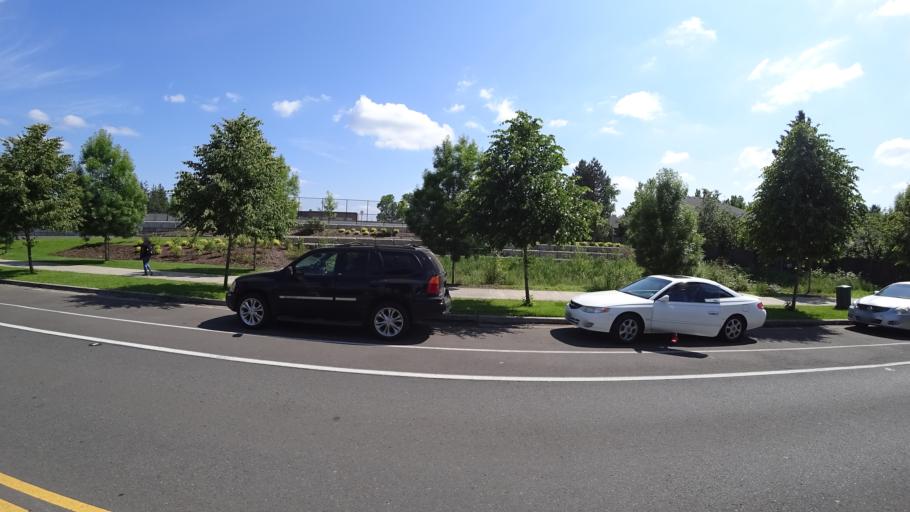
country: US
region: Oregon
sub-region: Washington County
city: Metzger
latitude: 45.4380
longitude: -122.7617
